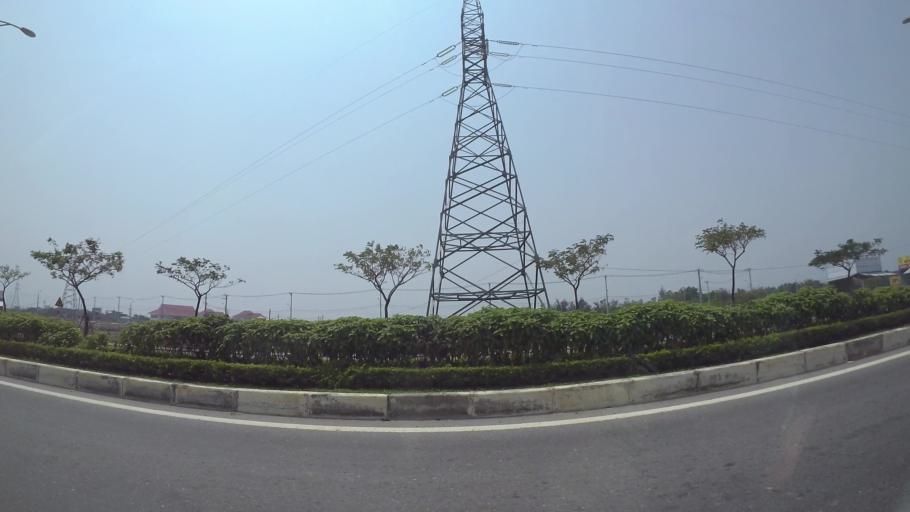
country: VN
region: Da Nang
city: Ngu Hanh Son
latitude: 15.9975
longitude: 108.2342
